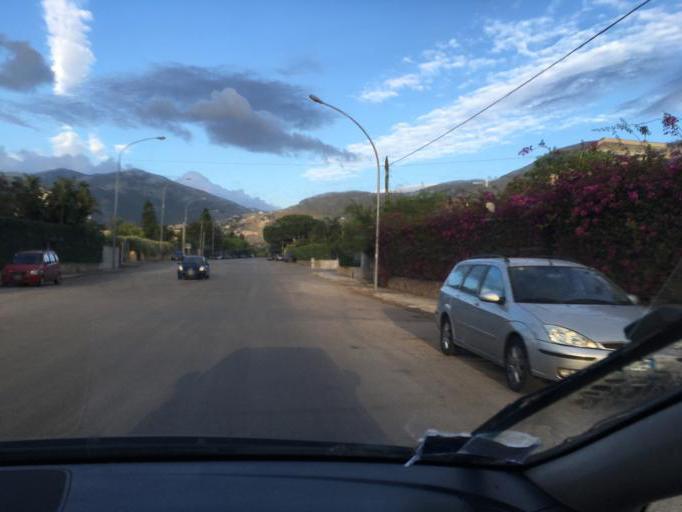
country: IT
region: Sicily
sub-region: Palermo
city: Palermo
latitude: 38.2035
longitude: 13.3210
